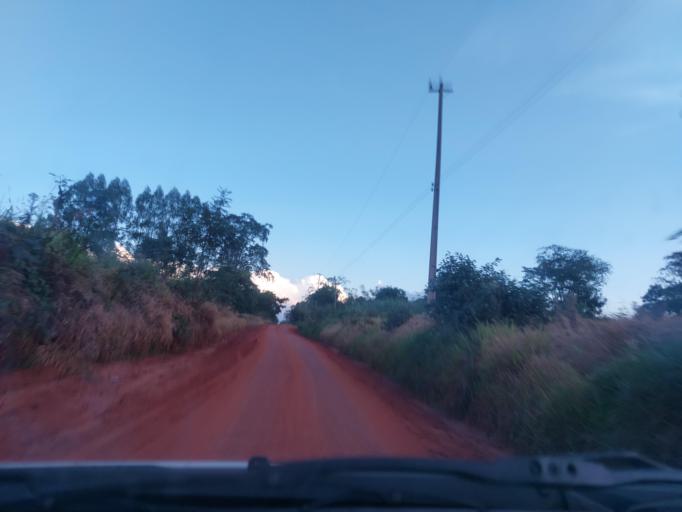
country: PY
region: San Pedro
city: Lima
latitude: -24.1461
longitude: -56.0114
